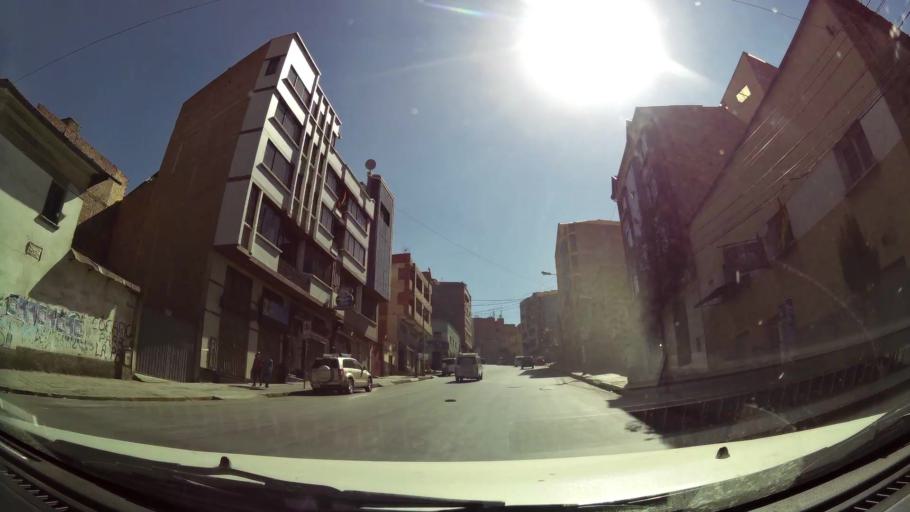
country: BO
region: La Paz
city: La Paz
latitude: -16.4936
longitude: -68.1550
